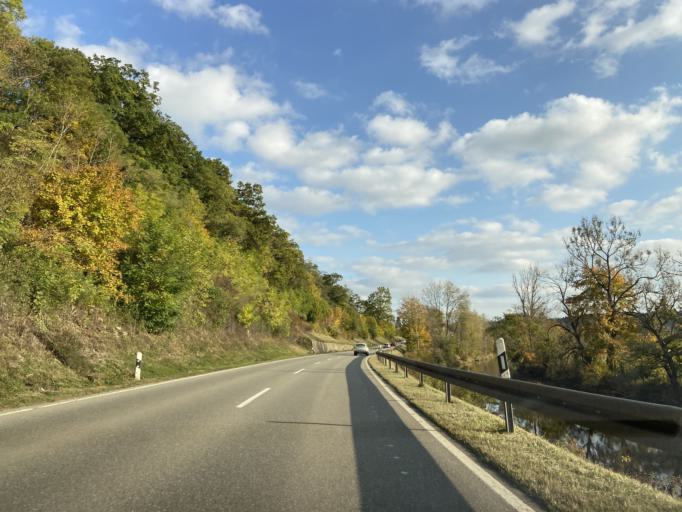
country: DE
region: Baden-Wuerttemberg
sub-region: Tuebingen Region
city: Sigmaringendorf
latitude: 48.0722
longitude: 9.2558
